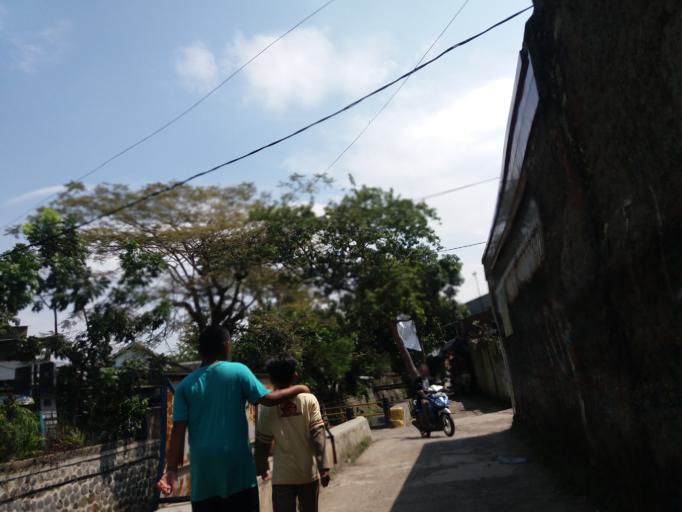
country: ID
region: West Java
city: Bandung
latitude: -6.9187
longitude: 107.6480
